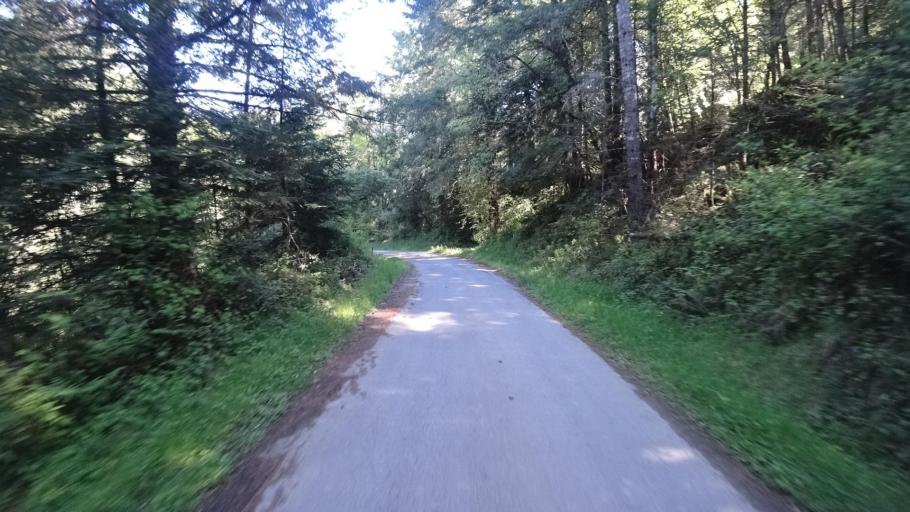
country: US
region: California
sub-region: Humboldt County
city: Ferndale
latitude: 40.5167
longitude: -124.1971
